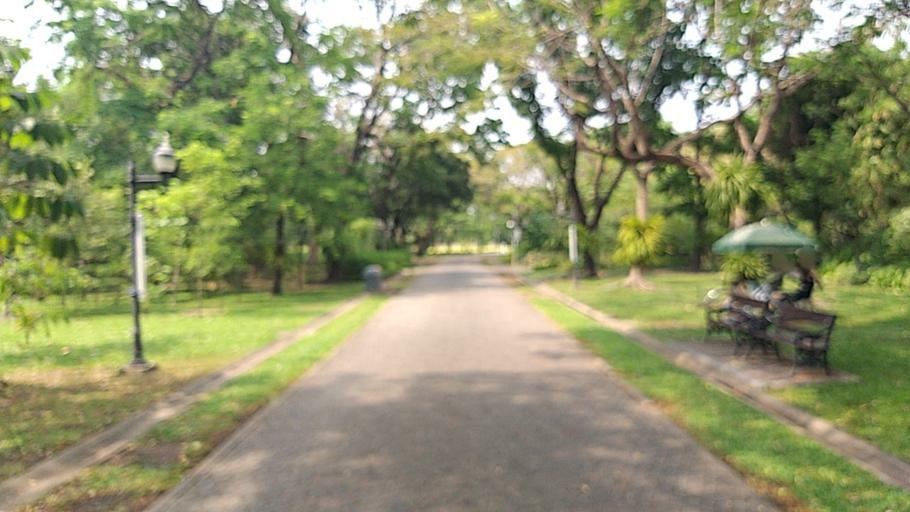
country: TH
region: Bangkok
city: Bang Sue
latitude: 13.8060
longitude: 100.5509
